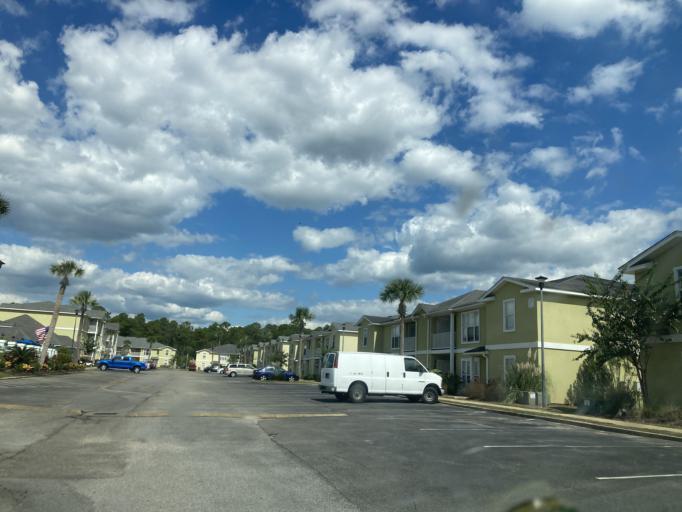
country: US
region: Mississippi
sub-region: Jackson County
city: Saint Martin
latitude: 30.4445
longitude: -88.8524
